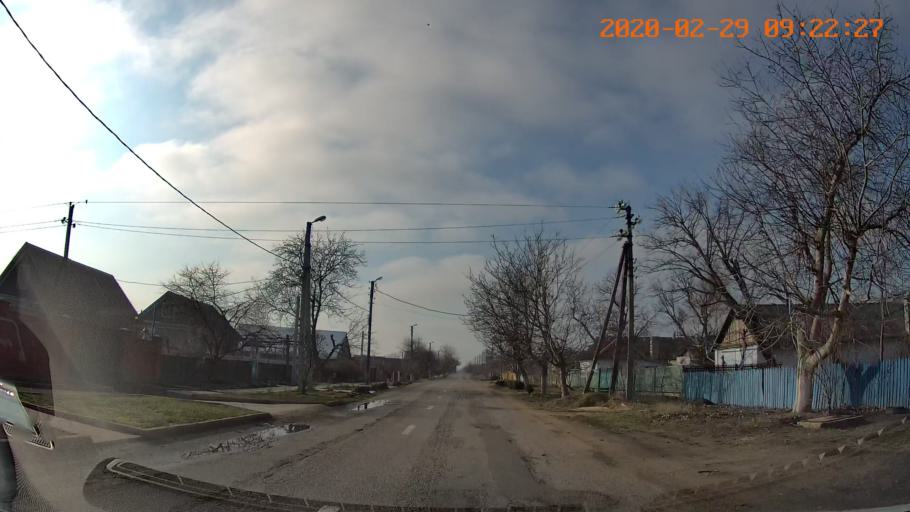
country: MD
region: Telenesti
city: Pervomaisc
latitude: 46.7352
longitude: 29.9641
